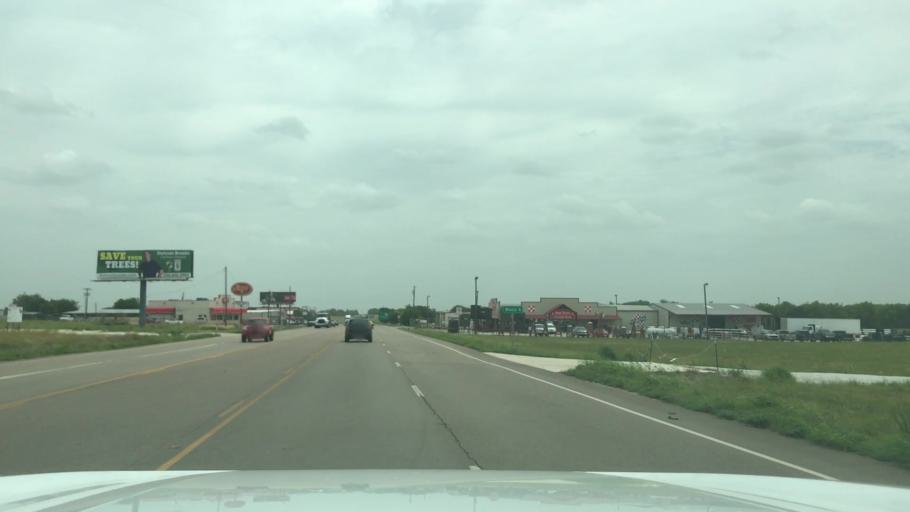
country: US
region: Texas
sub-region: McLennan County
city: Woodway
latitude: 31.5805
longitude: -97.3031
